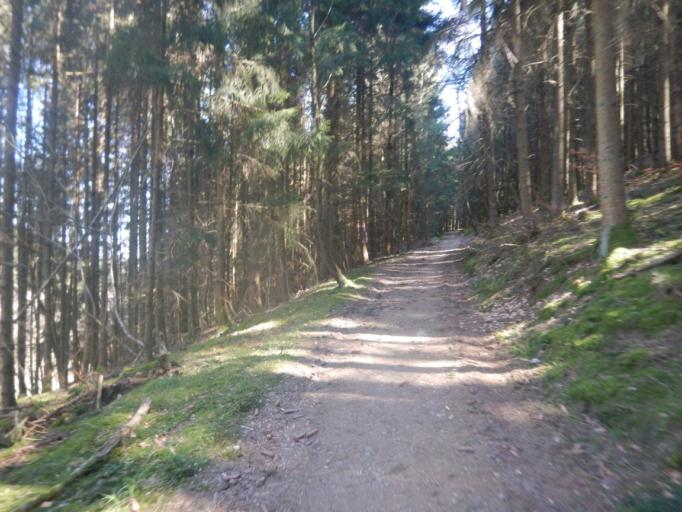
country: LU
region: Diekirch
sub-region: Canton de Wiltz
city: Wiltz
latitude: 49.9538
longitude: 5.9509
